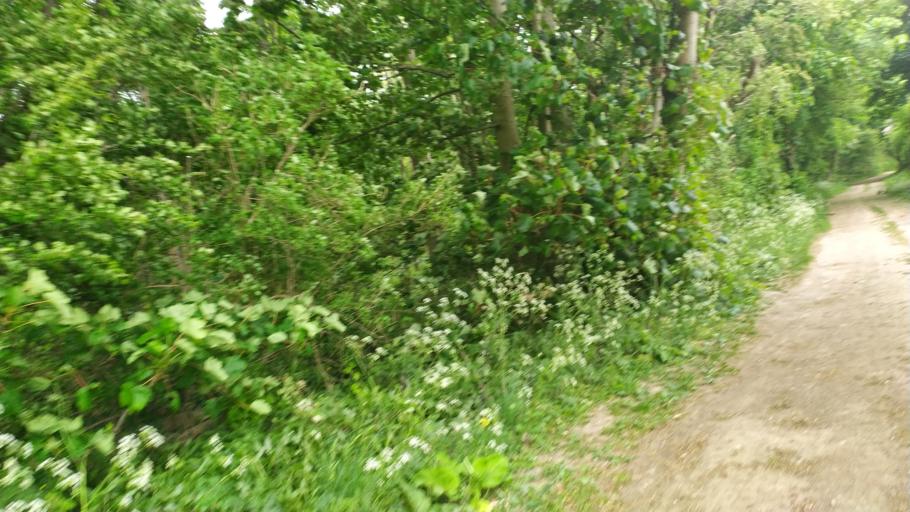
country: GB
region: England
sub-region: City and Borough of Leeds
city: Thorner
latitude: 53.8605
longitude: -1.3930
